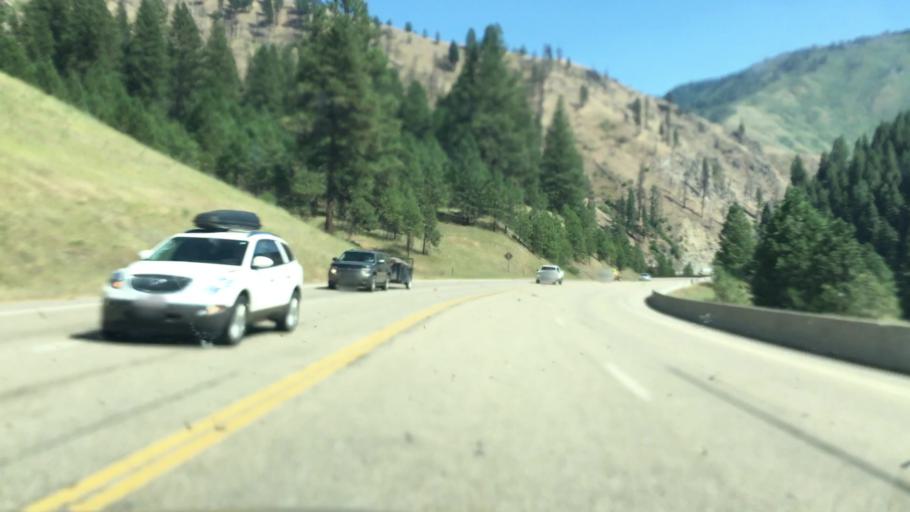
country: US
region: Idaho
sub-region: Boise County
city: Idaho City
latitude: 44.1109
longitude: -116.1005
